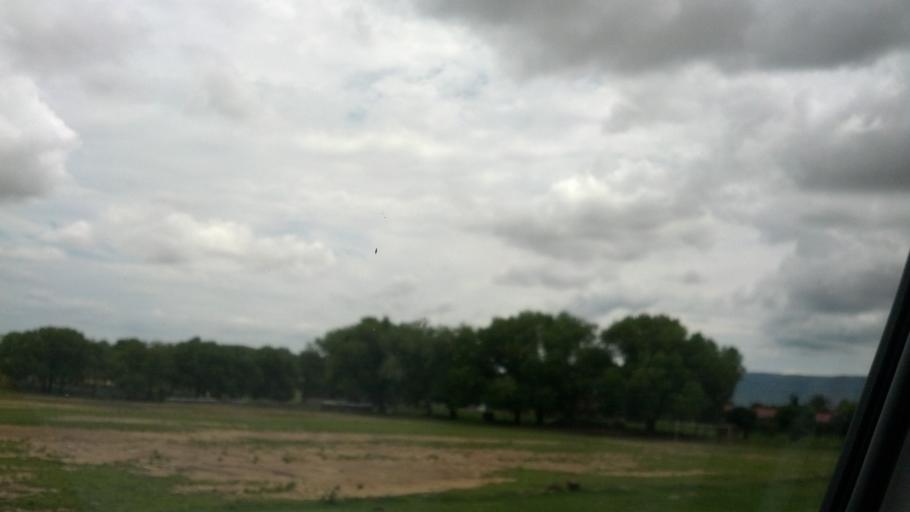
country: LS
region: Mafeteng
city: Mafeteng
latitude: -29.7018
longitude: 27.4305
